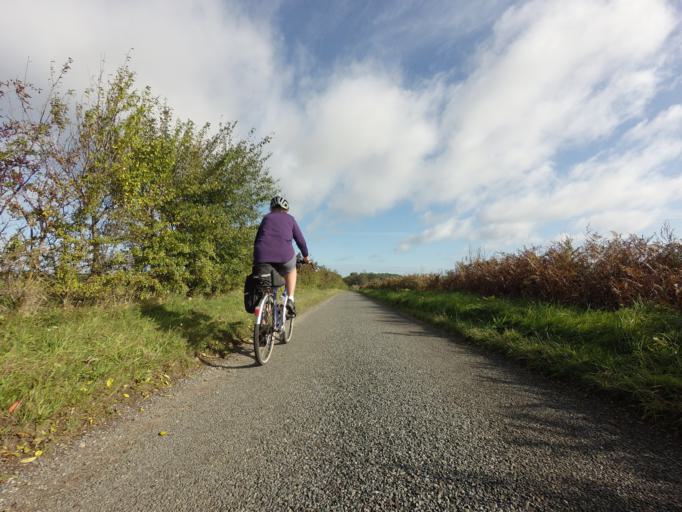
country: GB
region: England
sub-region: Norfolk
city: Dersingham
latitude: 52.8705
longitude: 0.6703
